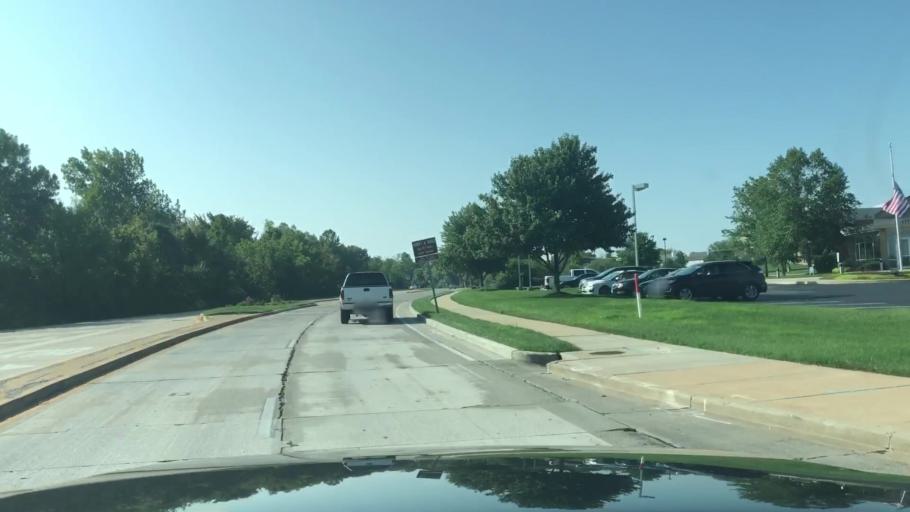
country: US
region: Missouri
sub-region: Saint Charles County
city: Saint Charles
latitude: 38.7755
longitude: -90.5275
